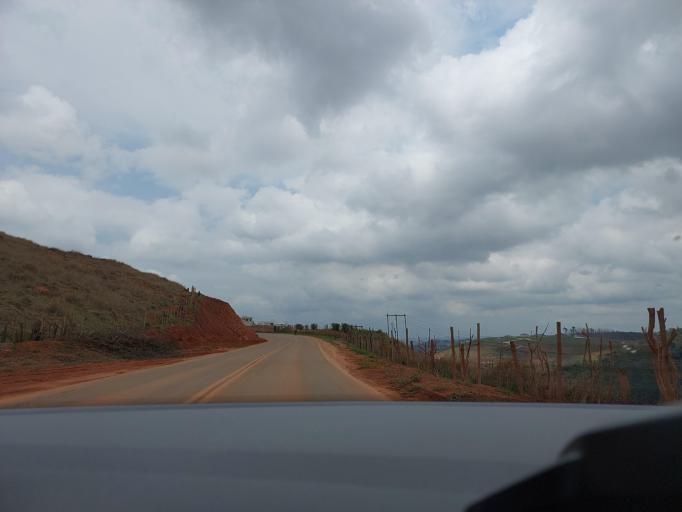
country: BR
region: Minas Gerais
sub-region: Ponte Nova
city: Ponte Nova
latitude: -20.3926
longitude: -42.8706
